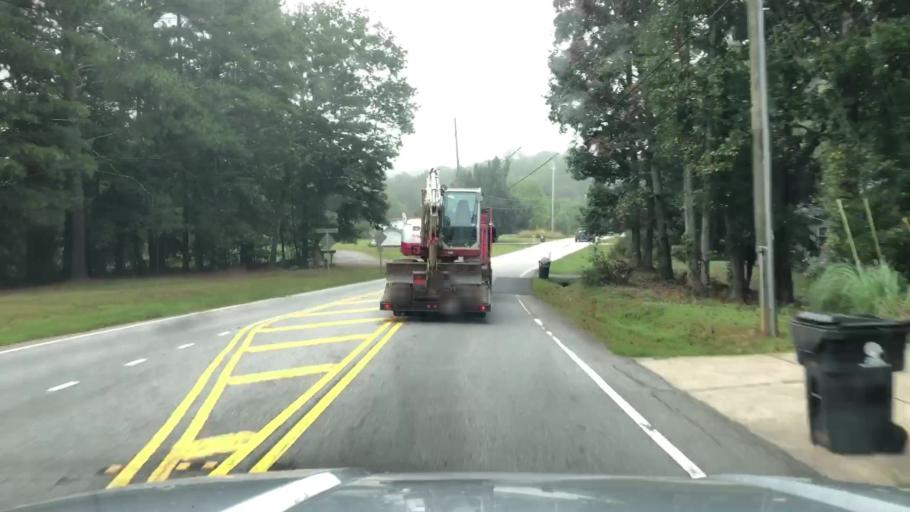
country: US
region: Georgia
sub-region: Bartow County
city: Emerson
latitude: 34.0459
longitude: -84.7766
